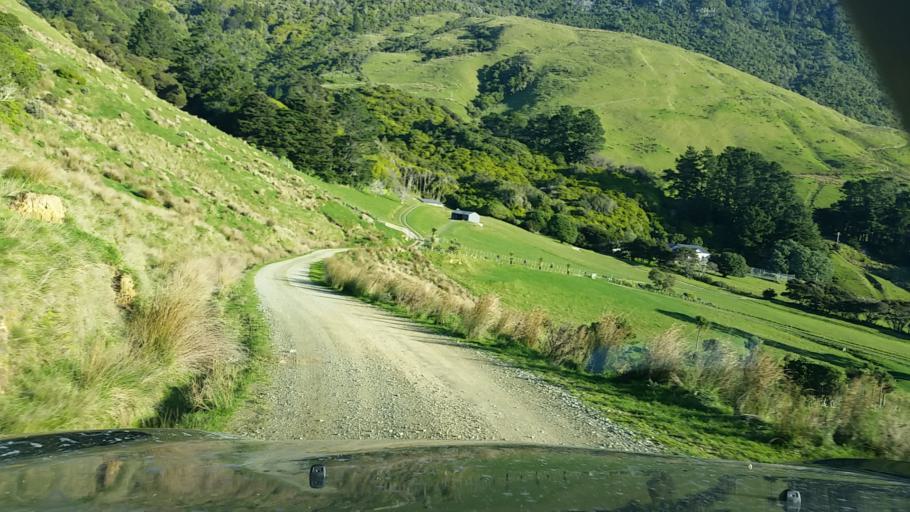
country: NZ
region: Marlborough
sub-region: Marlborough District
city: Picton
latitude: -41.0198
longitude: 174.1386
